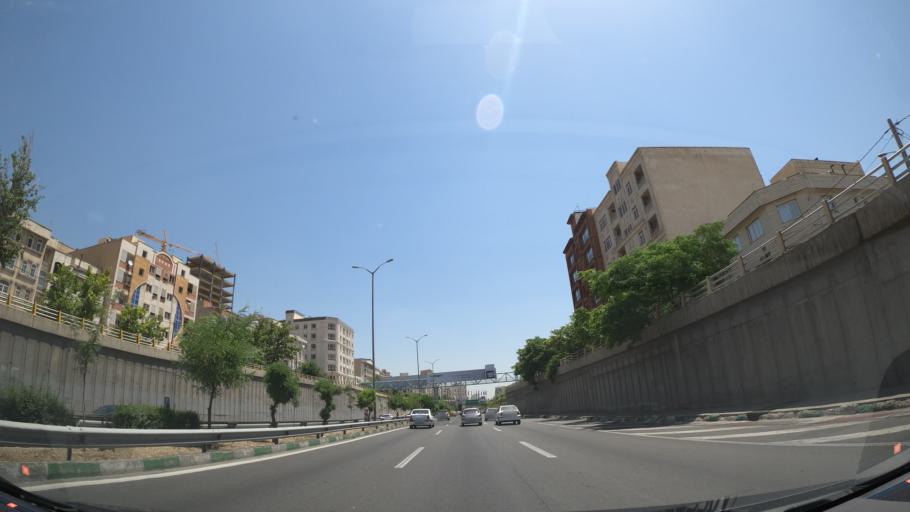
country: IR
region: Tehran
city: Tajrish
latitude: 35.7729
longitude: 51.3544
